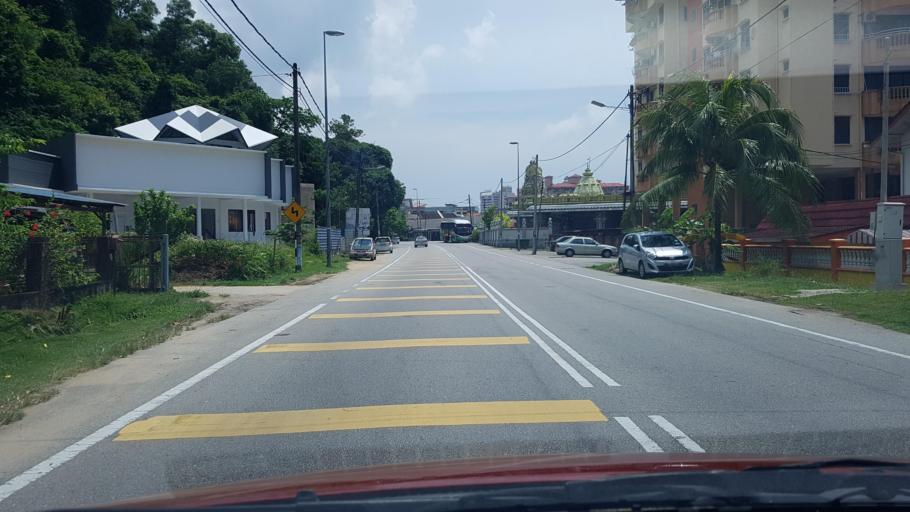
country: MY
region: Terengganu
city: Kuala Terengganu
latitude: 5.3217
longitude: 103.1393
